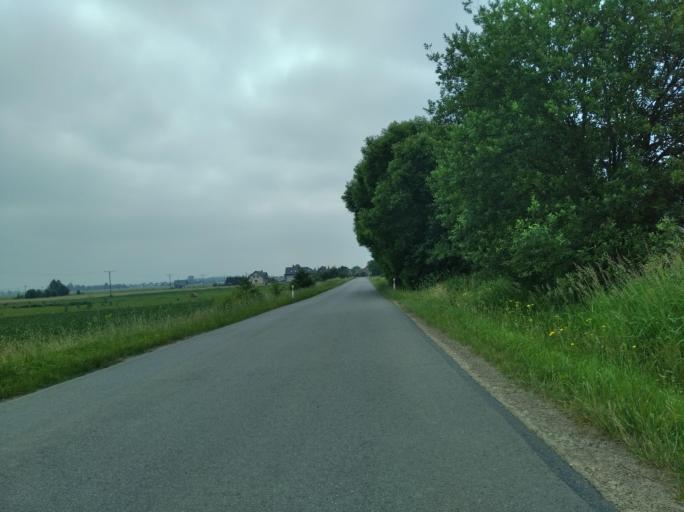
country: PL
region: Subcarpathian Voivodeship
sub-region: Powiat sanocki
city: Besko
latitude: 49.5957
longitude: 21.9307
